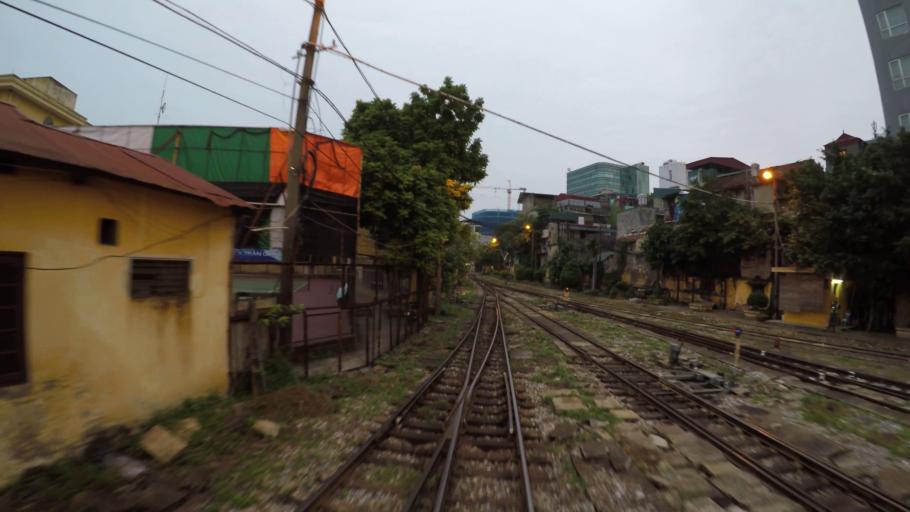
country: VN
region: Ha Noi
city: Hoan Kiem
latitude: 21.0309
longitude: 105.8450
